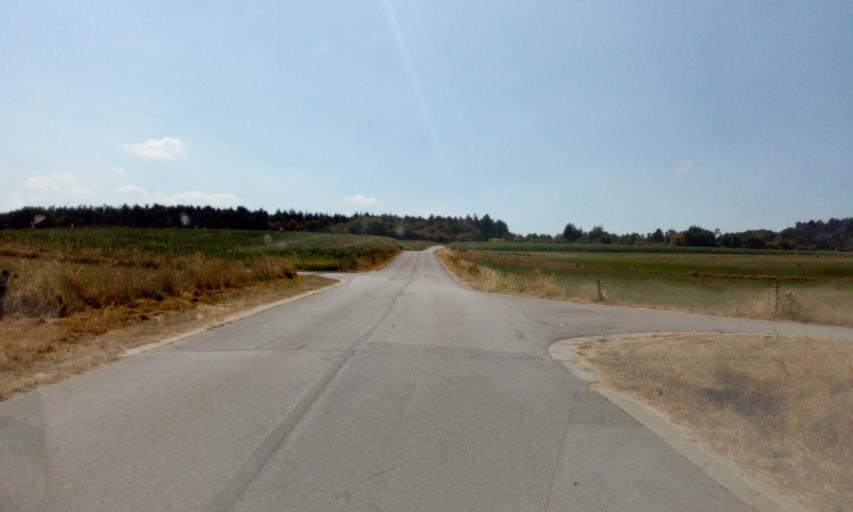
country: BE
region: Wallonia
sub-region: Province du Luxembourg
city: Wellin
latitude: 50.1223
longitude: 5.1454
